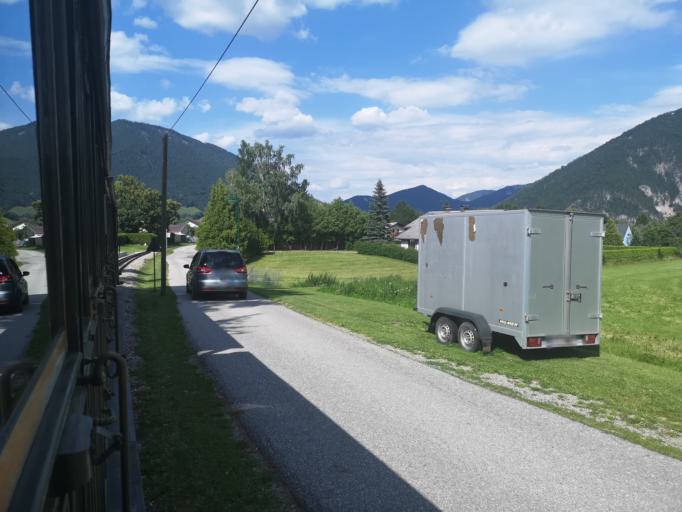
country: AT
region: Lower Austria
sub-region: Politischer Bezirk Neunkirchen
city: Puchberg am Schneeberg
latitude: 47.7846
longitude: 15.8988
